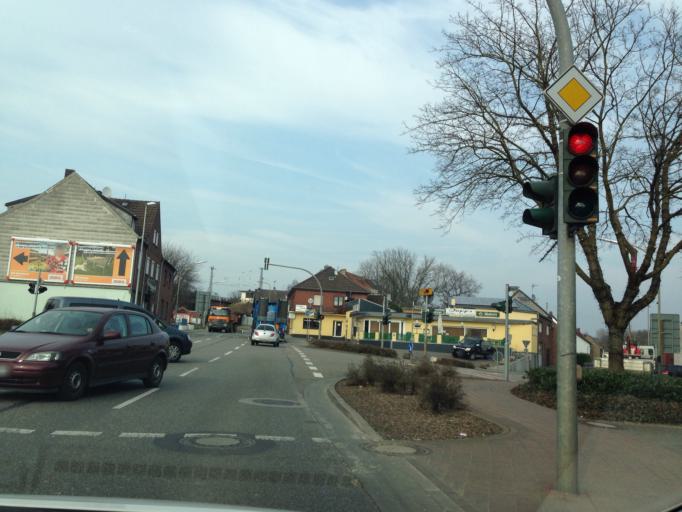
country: DE
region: North Rhine-Westphalia
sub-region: Regierungsbezirk Koln
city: Linnich
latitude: 51.0345
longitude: 6.2799
